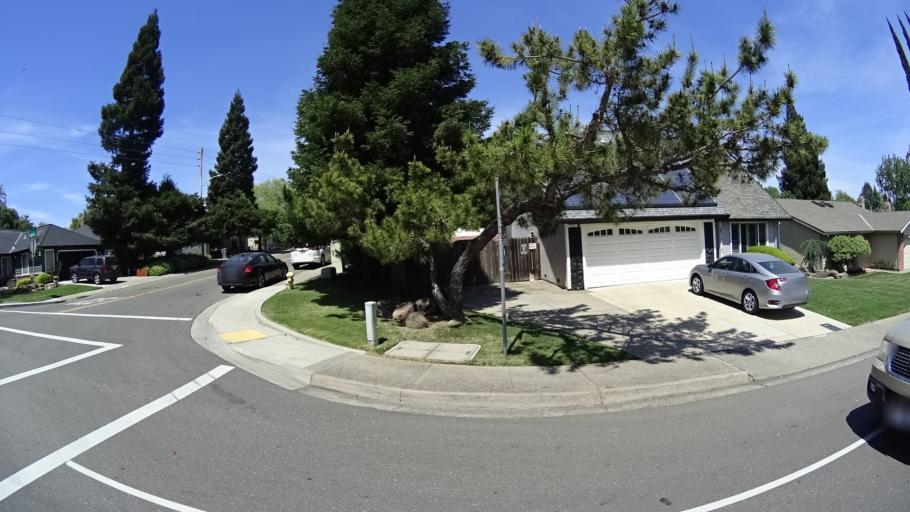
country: US
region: California
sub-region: Placer County
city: Rocklin
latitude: 38.7805
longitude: -121.2624
